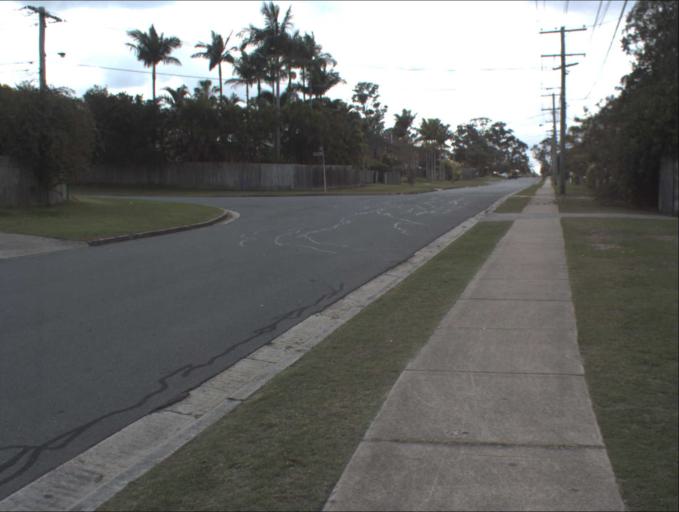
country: AU
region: Queensland
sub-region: Brisbane
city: Sunnybank Hills
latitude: -27.6620
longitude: 153.0494
